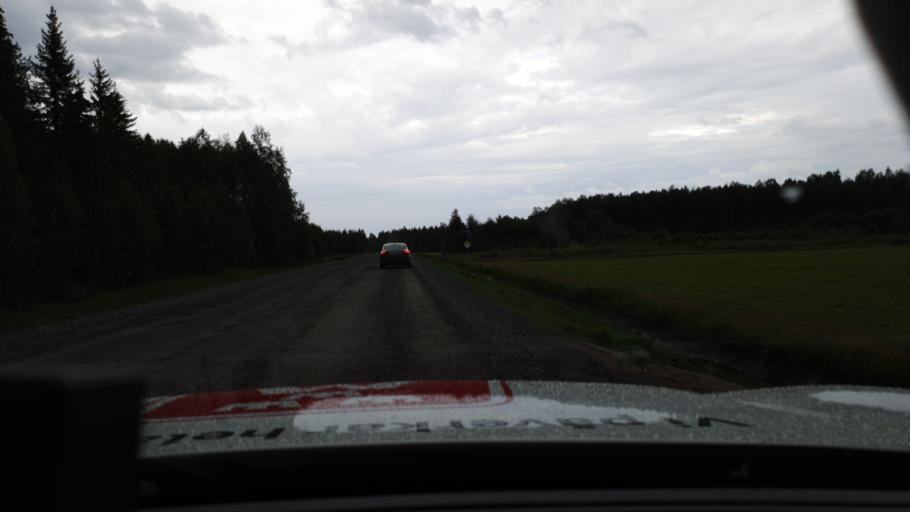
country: SE
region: Norrbotten
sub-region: Bodens Kommun
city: Boden
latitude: 65.8508
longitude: 21.5230
